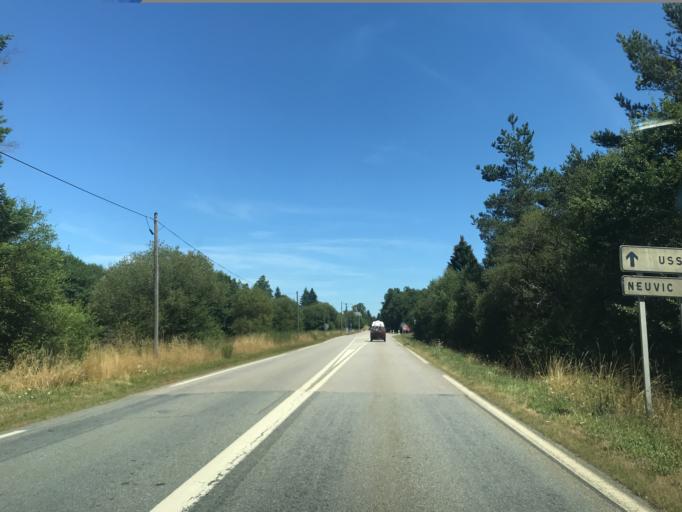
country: FR
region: Limousin
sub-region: Departement de la Correze
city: Meymac
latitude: 45.4985
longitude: 2.2234
